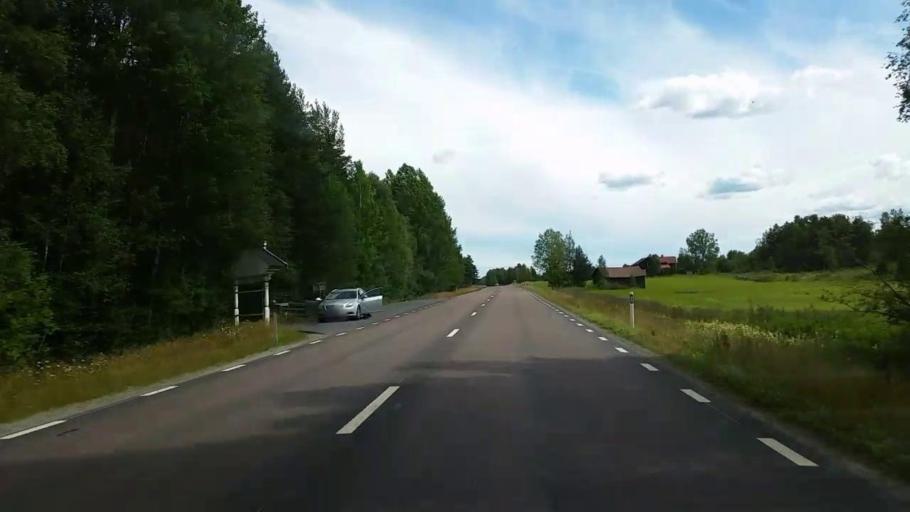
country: SE
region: Gaevleborg
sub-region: Ovanakers Kommun
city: Edsbyn
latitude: 61.3681
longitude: 15.8664
